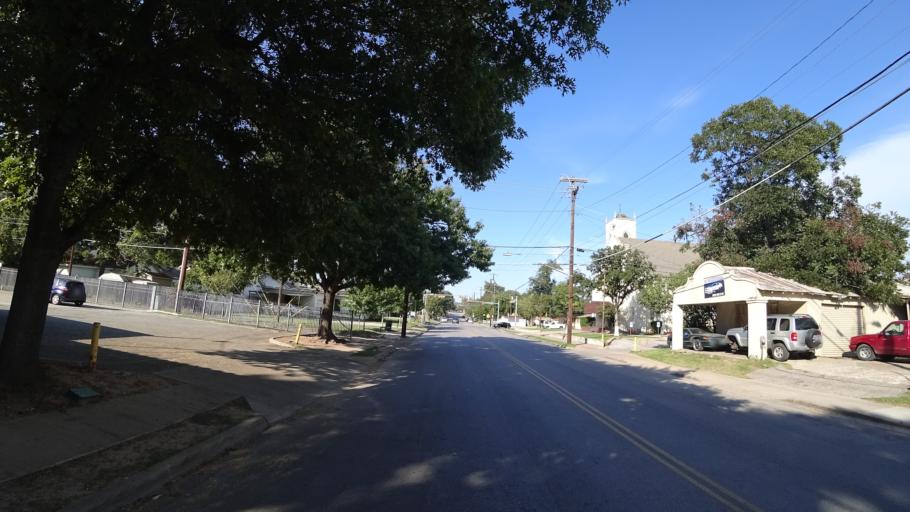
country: US
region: Texas
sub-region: Travis County
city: Austin
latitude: 30.2560
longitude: -97.7206
